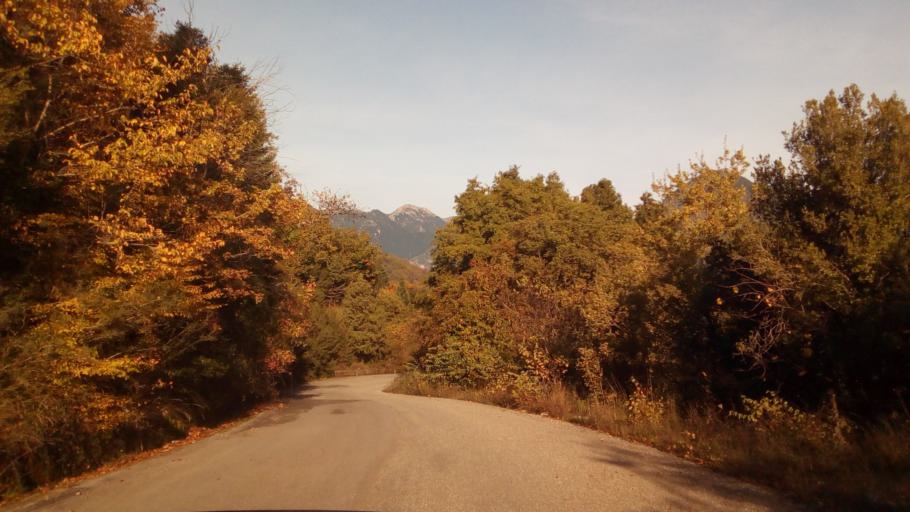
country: GR
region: West Greece
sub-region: Nomos Aitolias kai Akarnanias
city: Thermo
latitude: 38.6529
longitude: 21.8445
